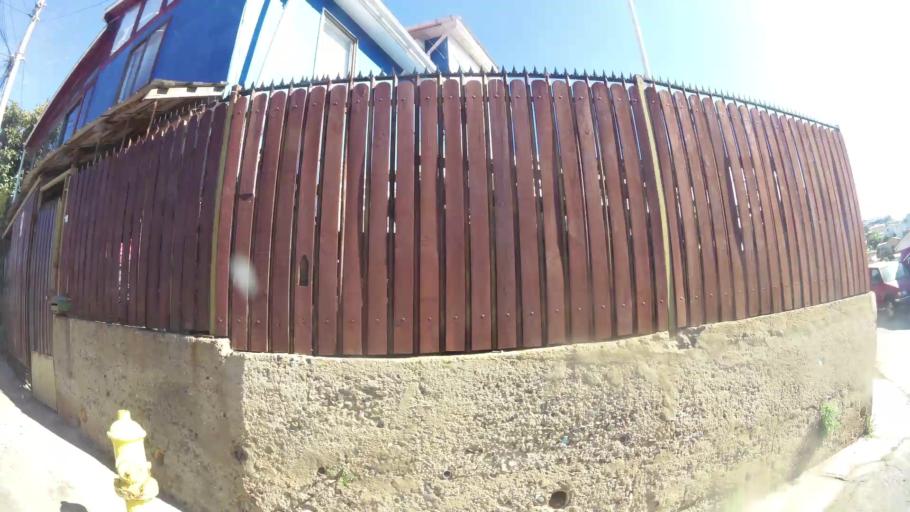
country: CL
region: Valparaiso
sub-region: Provincia de Valparaiso
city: Vina del Mar
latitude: -33.0392
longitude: -71.5646
